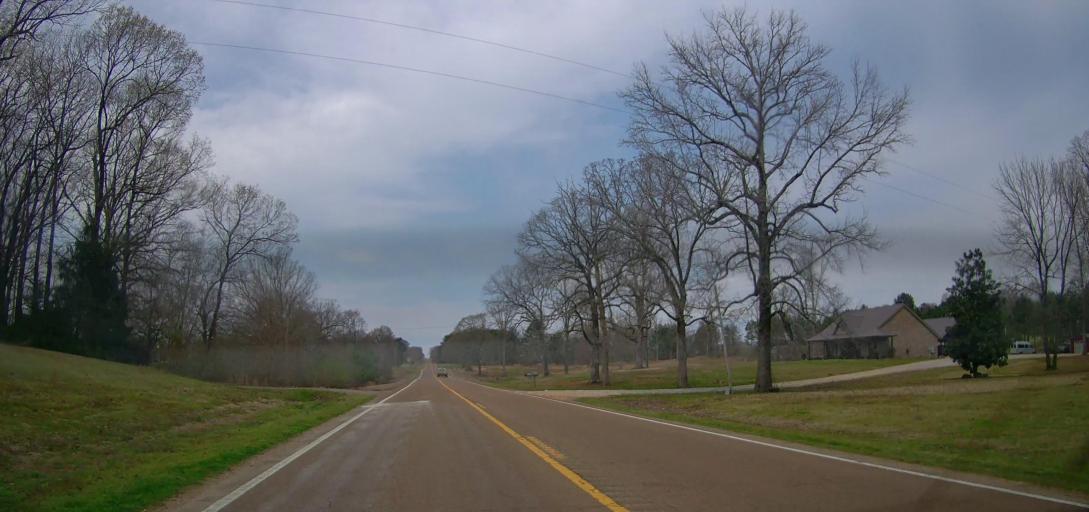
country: US
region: Mississippi
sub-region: Marshall County
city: Byhalia
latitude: 34.8309
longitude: -89.5730
